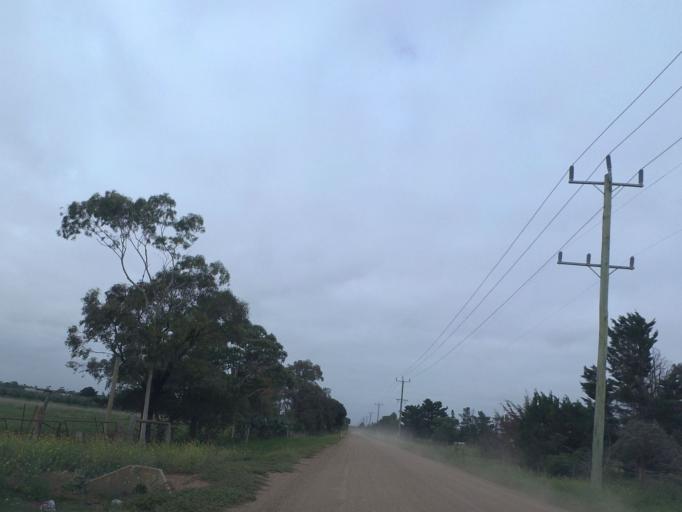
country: AU
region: Victoria
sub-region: Melton
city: Kurunjang
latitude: -37.6971
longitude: 144.6219
